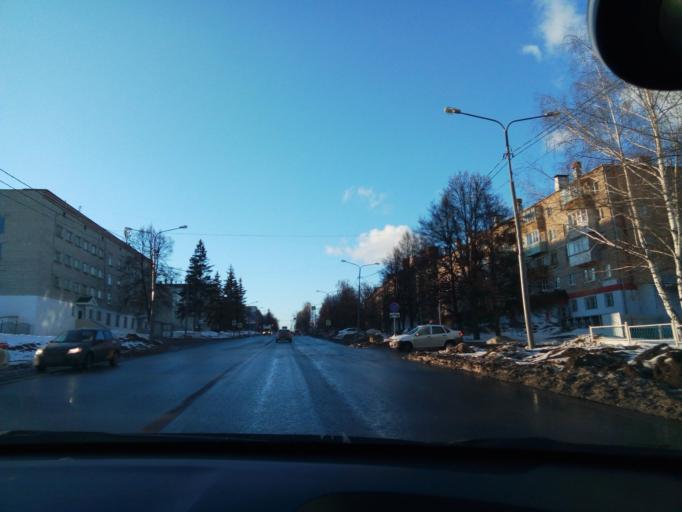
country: RU
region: Chuvashia
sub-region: Cheboksarskiy Rayon
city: Cheboksary
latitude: 56.1389
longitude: 47.2004
